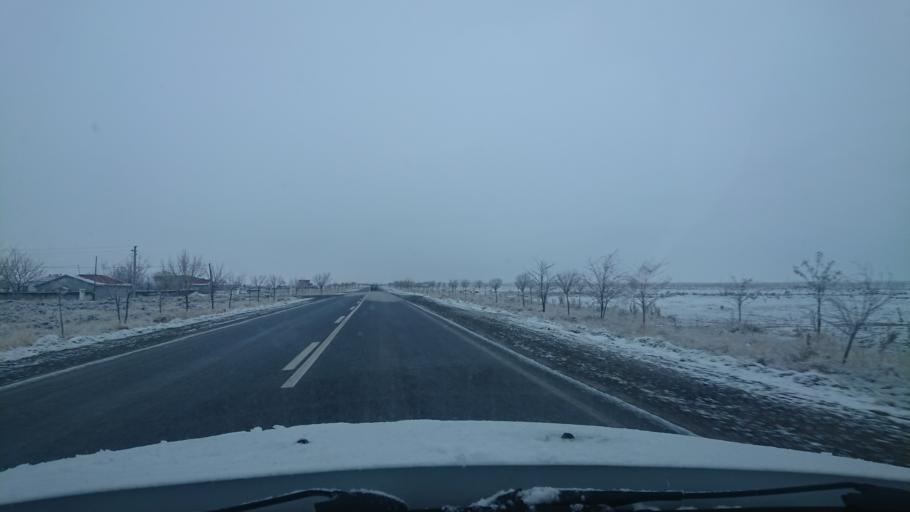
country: TR
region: Aksaray
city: Yesilova
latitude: 38.3037
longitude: 33.7560
